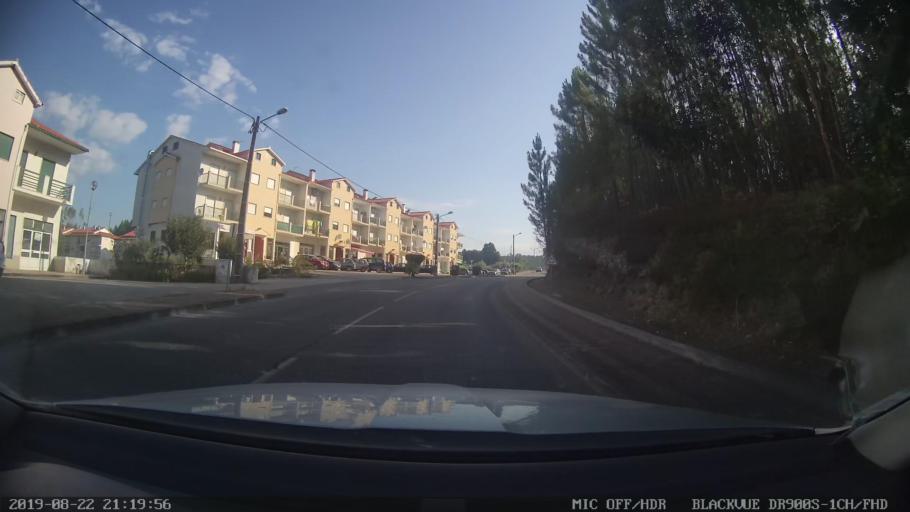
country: PT
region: Castelo Branco
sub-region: Serta
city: Serta
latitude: 39.8100
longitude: -8.1077
